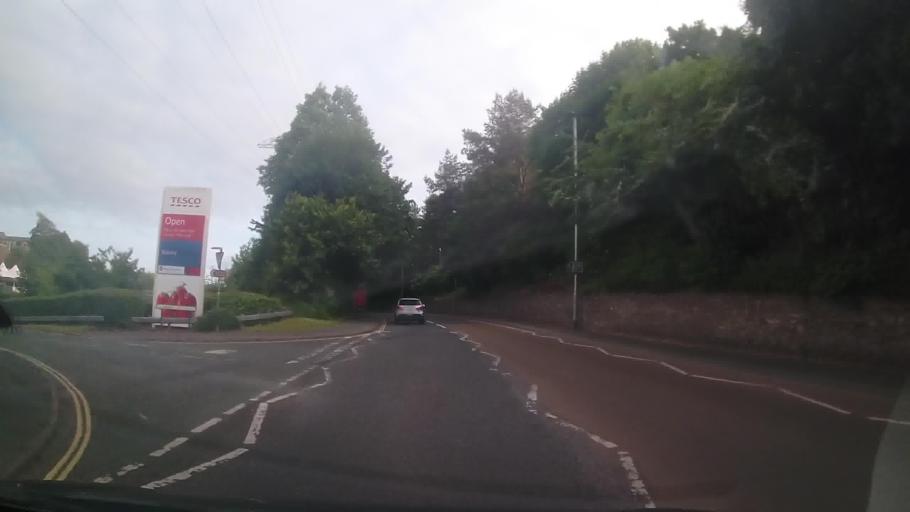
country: GB
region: England
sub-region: Devon
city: Kingsbridge
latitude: 50.2874
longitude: -3.7803
